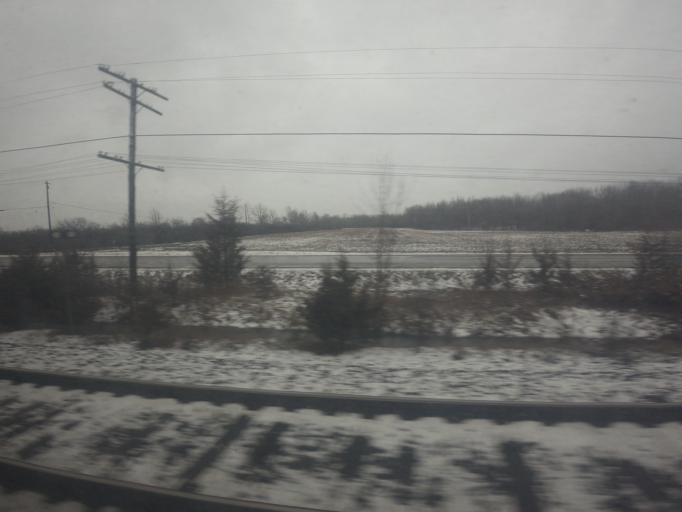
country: CA
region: Ontario
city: Belleville
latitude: 44.1578
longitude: -77.4517
